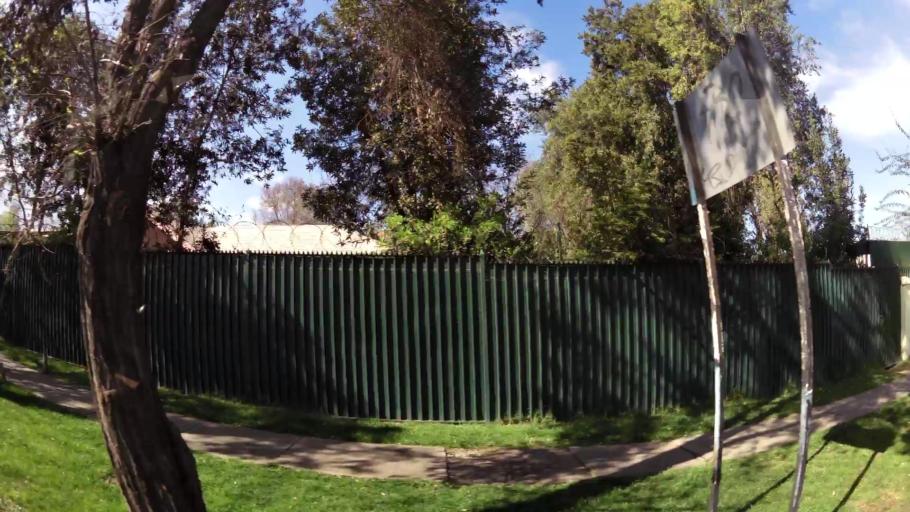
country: CL
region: Santiago Metropolitan
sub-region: Provincia de Santiago
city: Villa Presidente Frei, Nunoa, Santiago, Chile
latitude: -33.4448
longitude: -70.5528
